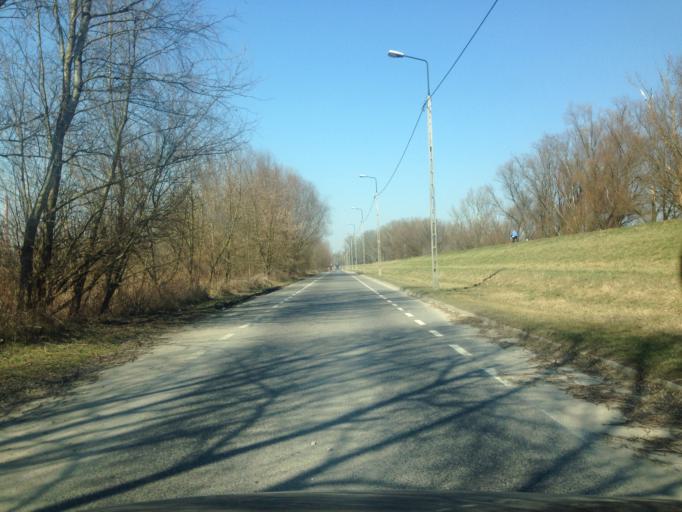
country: PL
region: Masovian Voivodeship
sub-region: Warszawa
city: Wilanow
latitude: 52.1829
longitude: 21.1107
